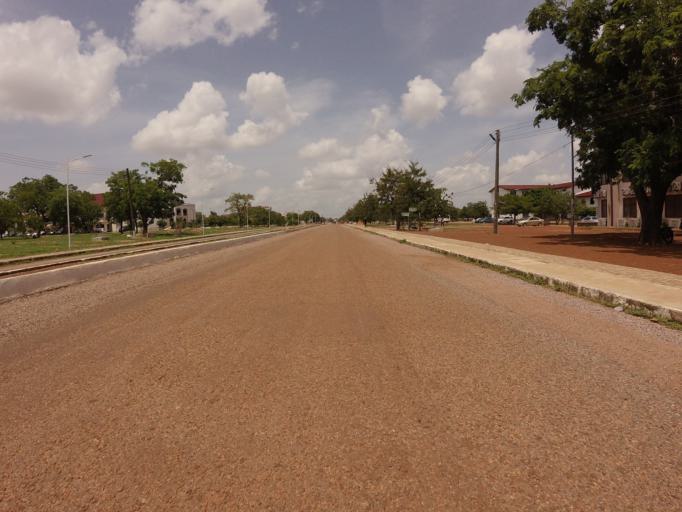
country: GH
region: Northern
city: Tamale
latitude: 9.3737
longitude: -0.8865
